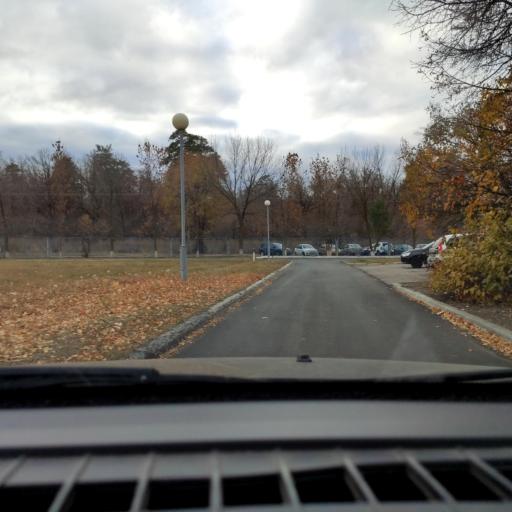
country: RU
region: Samara
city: Tol'yatti
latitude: 53.5209
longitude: 49.3270
